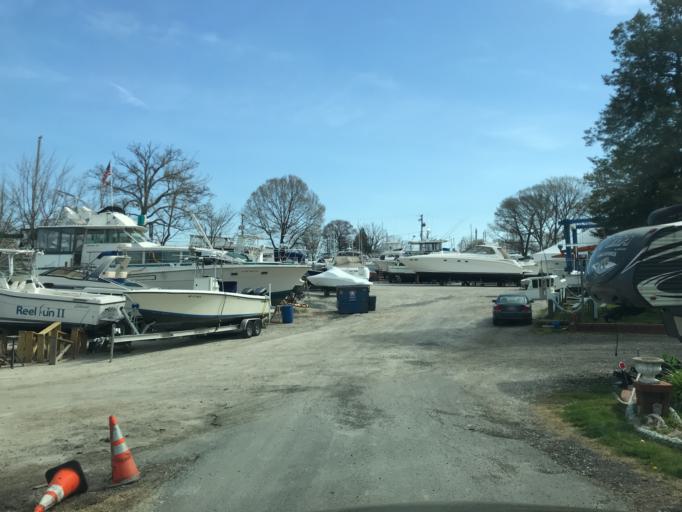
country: US
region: Maryland
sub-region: Baltimore County
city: Middle River
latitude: 39.3095
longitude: -76.4316
